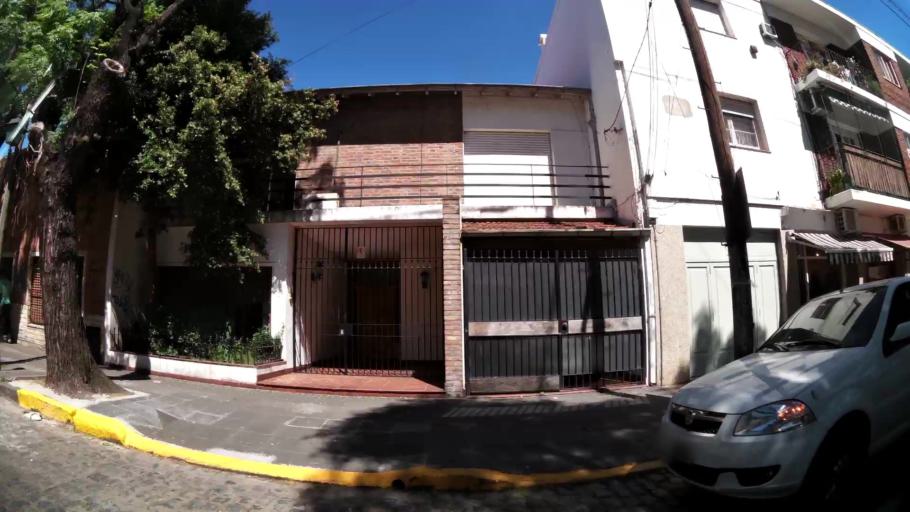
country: AR
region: Buenos Aires
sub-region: Partido de San Isidro
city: San Isidro
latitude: -34.4700
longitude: -58.5149
